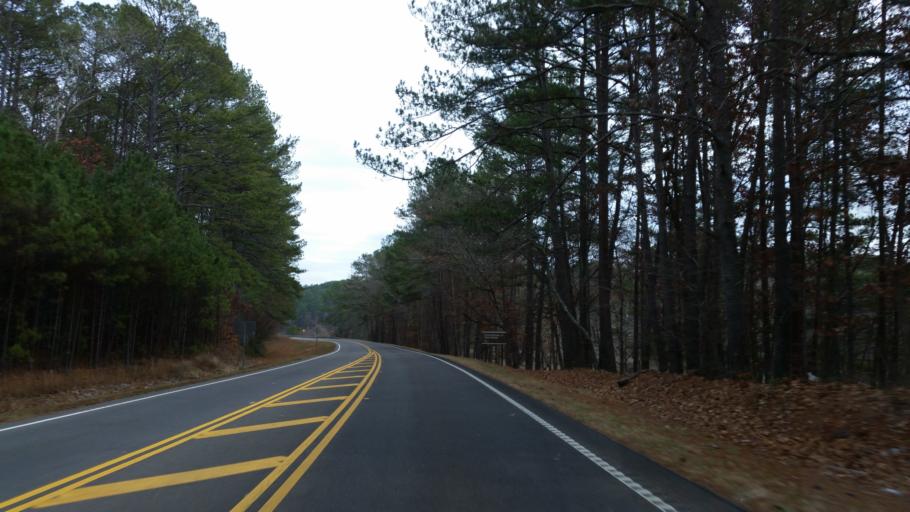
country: US
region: Georgia
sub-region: Cherokee County
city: Holly Springs
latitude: 34.2158
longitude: -84.5700
